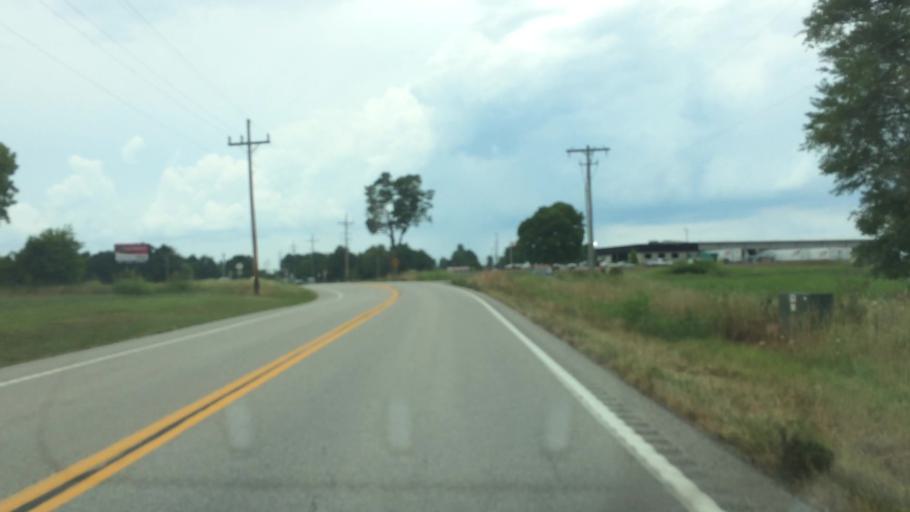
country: US
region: Missouri
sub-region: Greene County
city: Strafford
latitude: 37.2616
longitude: -93.1351
